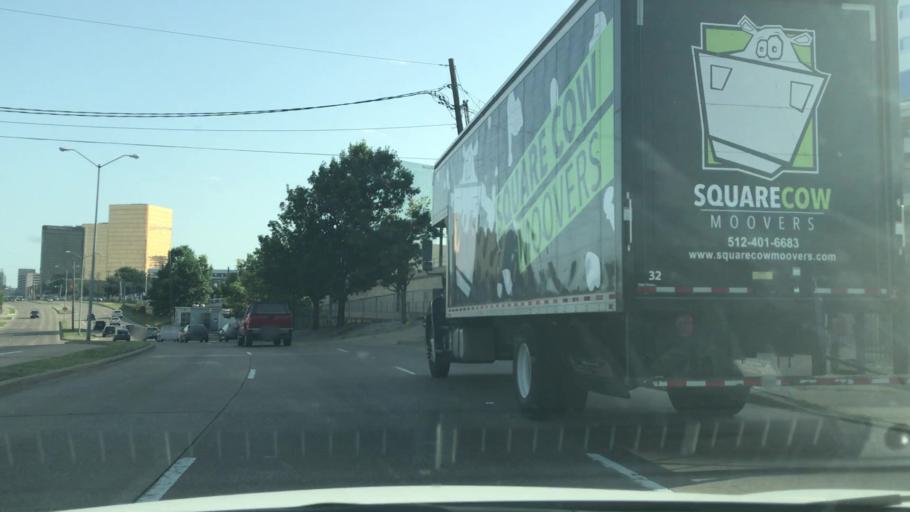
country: US
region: Texas
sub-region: Dallas County
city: University Park
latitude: 32.8707
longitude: -96.7655
